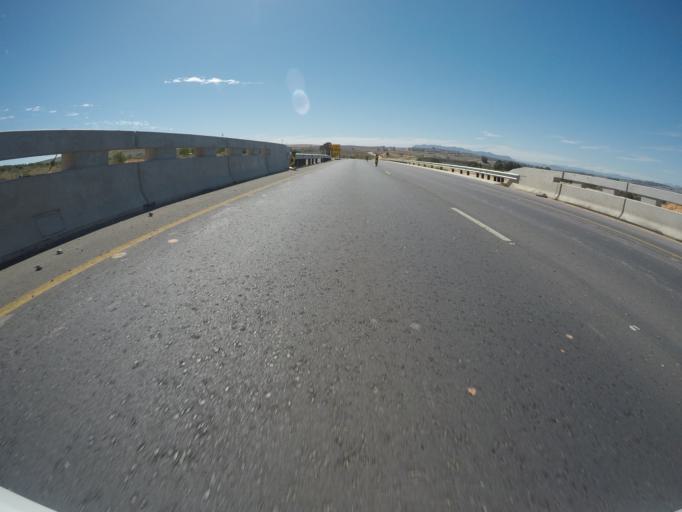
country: ZA
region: Western Cape
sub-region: West Coast District Municipality
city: Malmesbury
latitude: -33.4873
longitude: 18.6725
